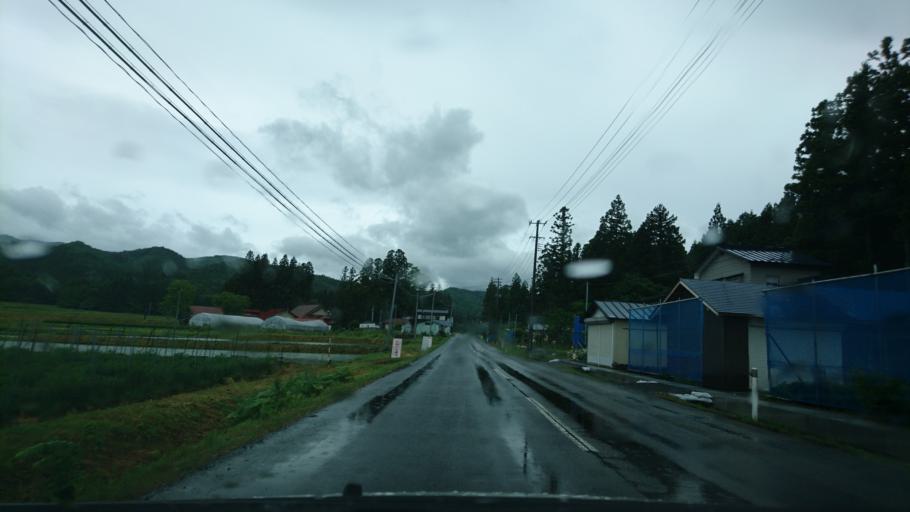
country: JP
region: Iwate
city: Ichinoseki
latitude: 38.9820
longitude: 140.9168
